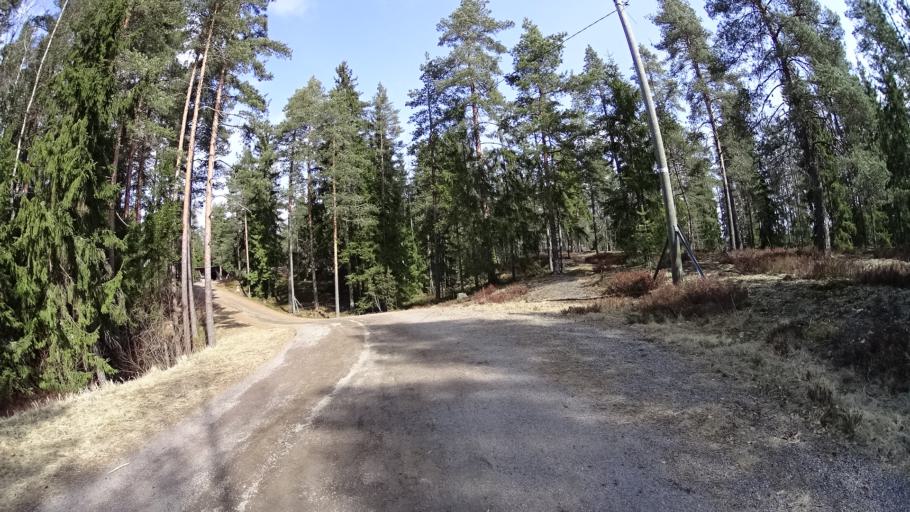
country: FI
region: Uusimaa
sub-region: Helsinki
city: Kilo
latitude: 60.3027
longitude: 24.8137
